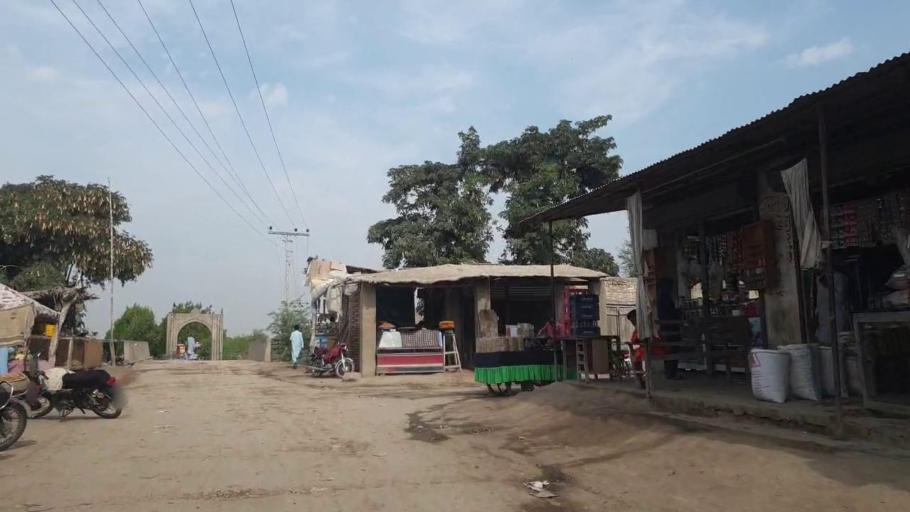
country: PK
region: Sindh
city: Rajo Khanani
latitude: 24.9561
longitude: 68.9779
